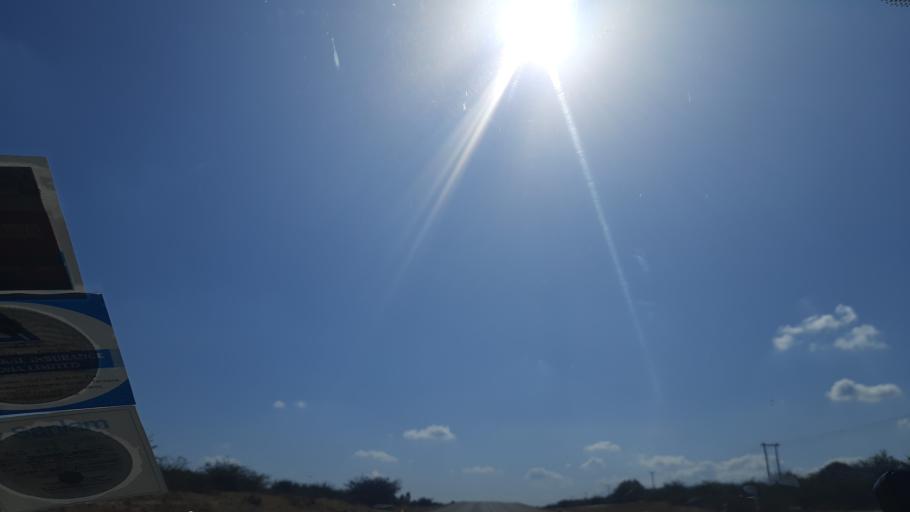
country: TZ
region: Singida
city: Kilimatinde
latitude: -5.7267
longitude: 34.7883
